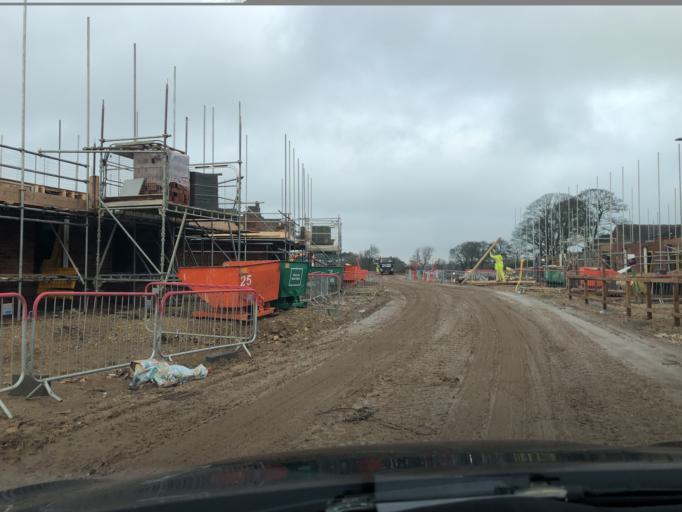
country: GB
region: England
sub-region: North Yorkshire
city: Stokesley
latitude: 54.4693
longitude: -1.2031
